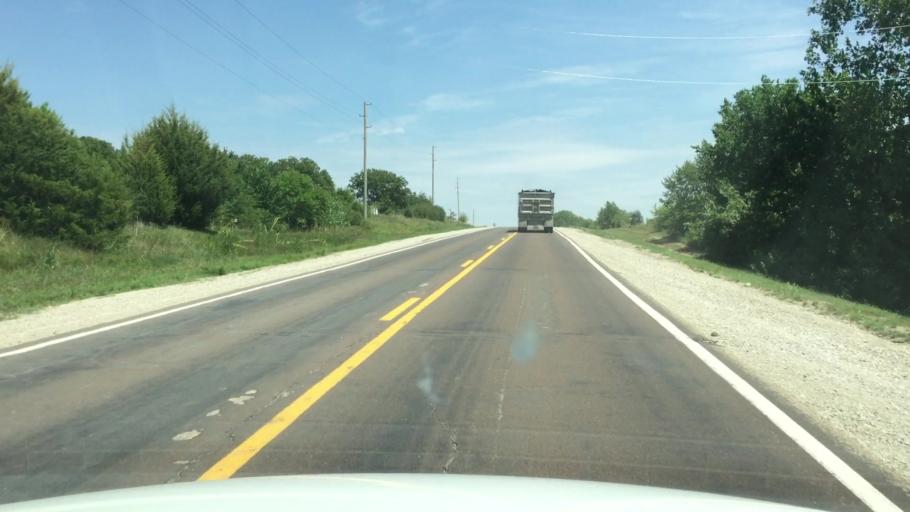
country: US
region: Kansas
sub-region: Shawnee County
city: Topeka
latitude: 38.9859
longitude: -95.5156
